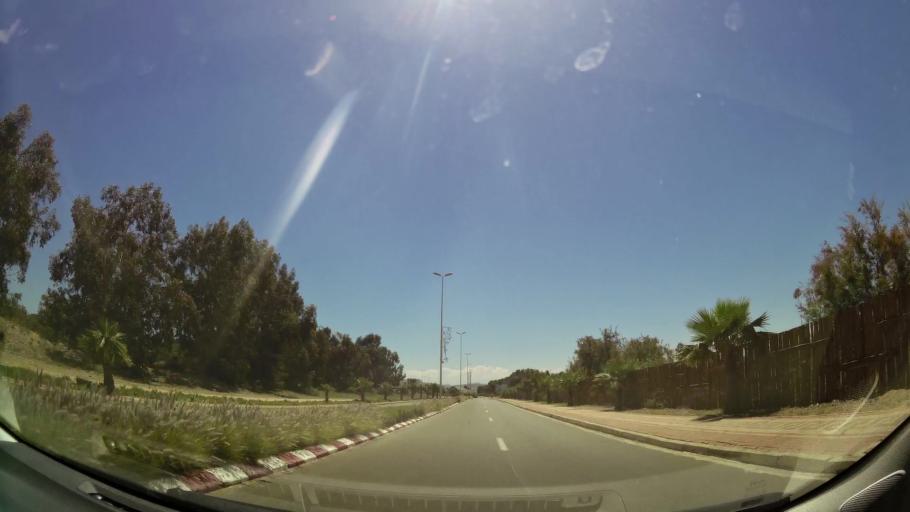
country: MA
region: Oriental
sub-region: Berkane-Taourirt
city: Madagh
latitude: 35.0940
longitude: -2.2677
